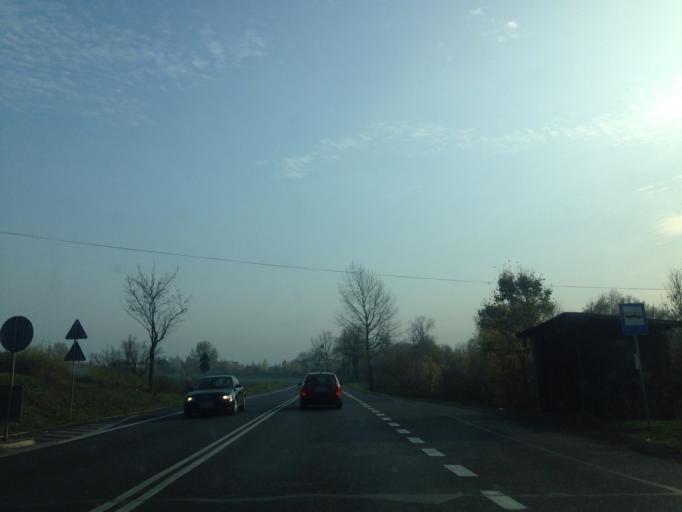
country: PL
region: Kujawsko-Pomorskie
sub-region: Powiat chelminski
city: Chelmno
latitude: 53.3354
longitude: 18.4693
